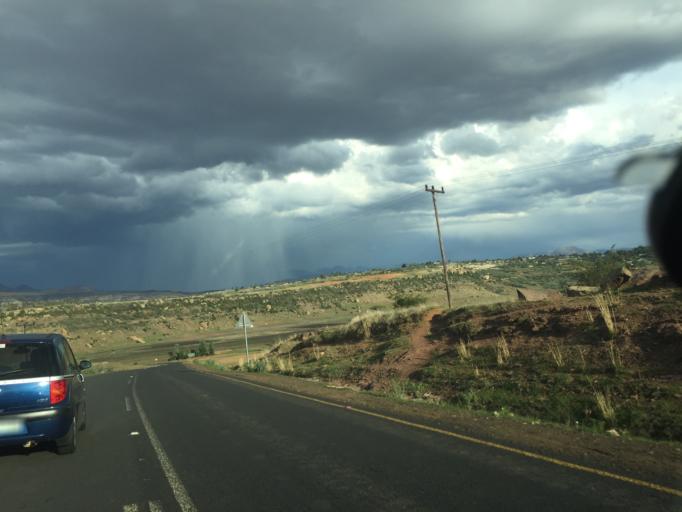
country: LS
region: Berea
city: Teyateyaneng
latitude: -29.0916
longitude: 27.9381
